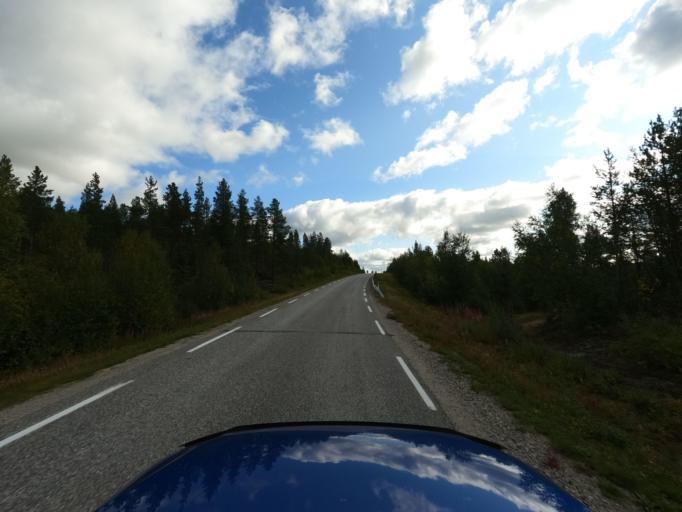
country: NO
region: Finnmark Fylke
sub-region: Karasjok
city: Karasjohka
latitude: 69.4435
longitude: 25.2463
